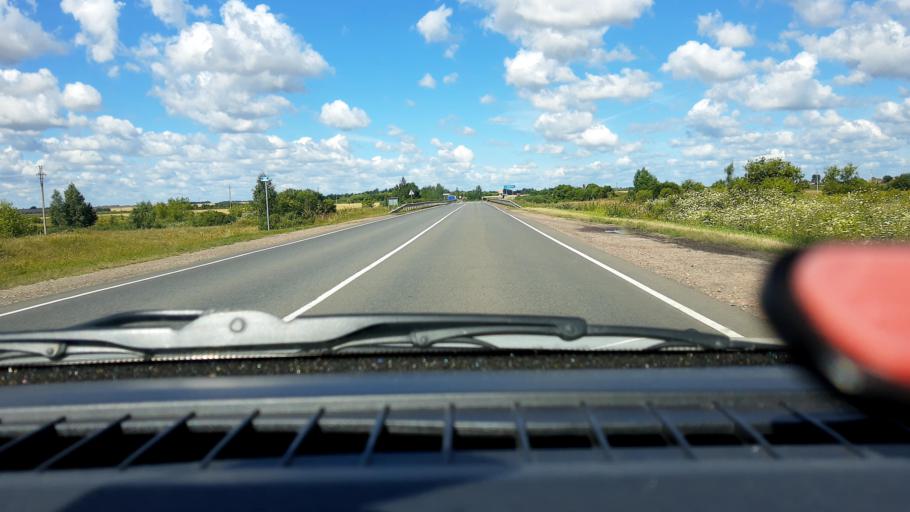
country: RU
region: Nizjnij Novgorod
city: Shatki
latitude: 55.2444
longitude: 44.0141
